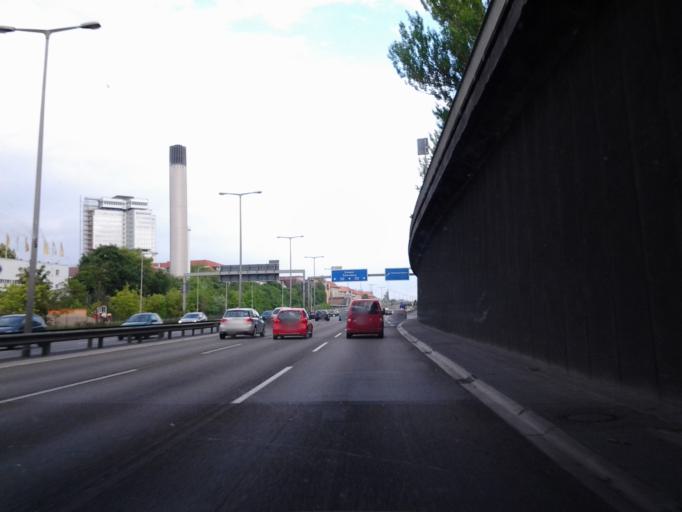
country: DE
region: Berlin
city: Halensee
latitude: 52.4916
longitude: 13.2945
